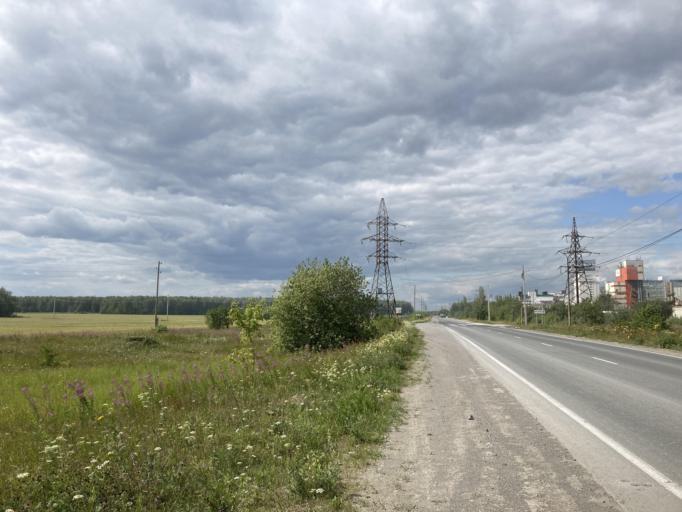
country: RU
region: Sverdlovsk
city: Bogdanovich
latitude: 56.8005
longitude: 62.0382
